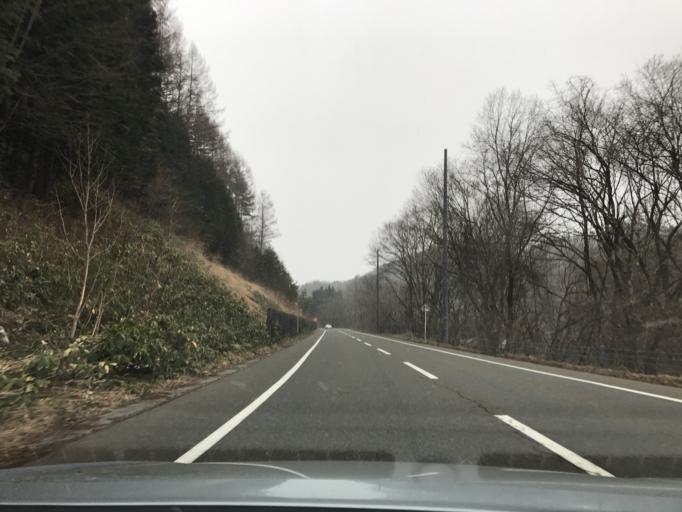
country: JP
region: Nagano
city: Omachi
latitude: 36.5385
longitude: 137.8647
